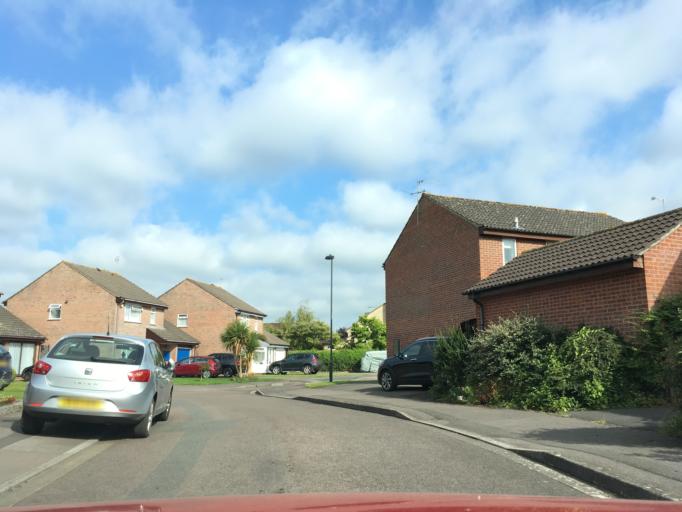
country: GB
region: England
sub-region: South Gloucestershire
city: Chipping Sodbury
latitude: 51.5411
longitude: -2.3876
